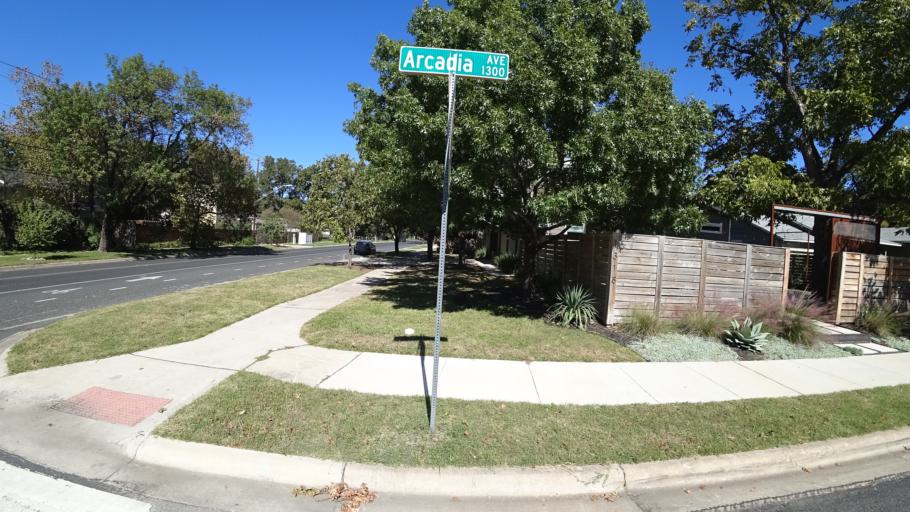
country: US
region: Texas
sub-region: Travis County
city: Austin
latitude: 30.3350
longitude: -97.7297
